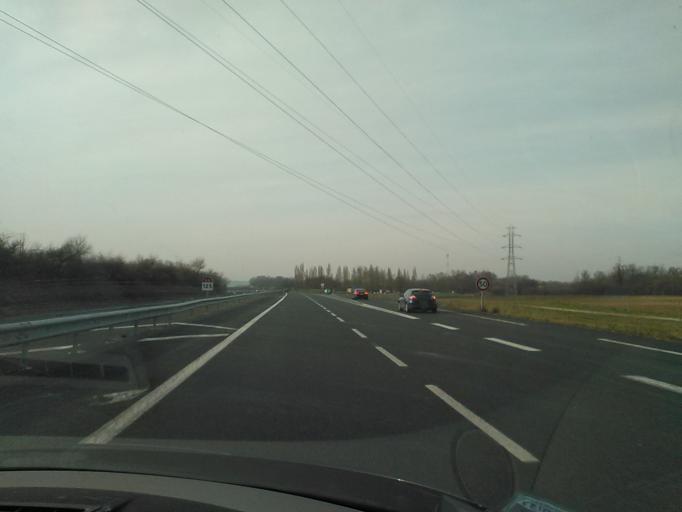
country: FR
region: Champagne-Ardenne
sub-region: Departement de l'Aube
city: Saint-Pouange
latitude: 48.2302
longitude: 4.0585
